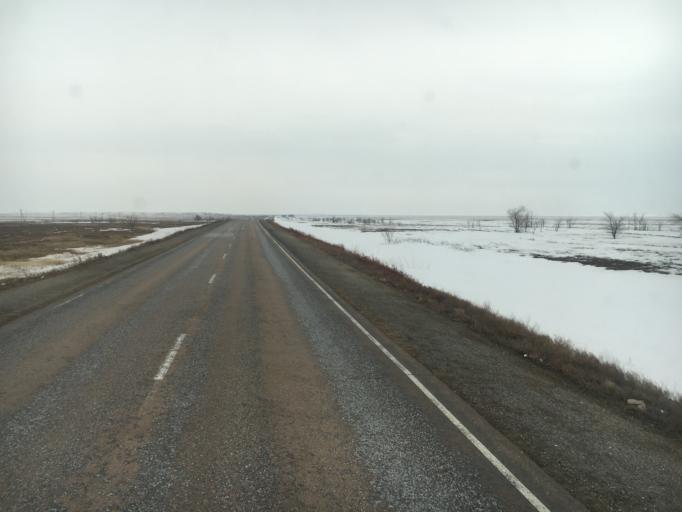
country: RU
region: Orenburg
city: Dombarovskiy
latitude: 50.0934
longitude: 59.4919
